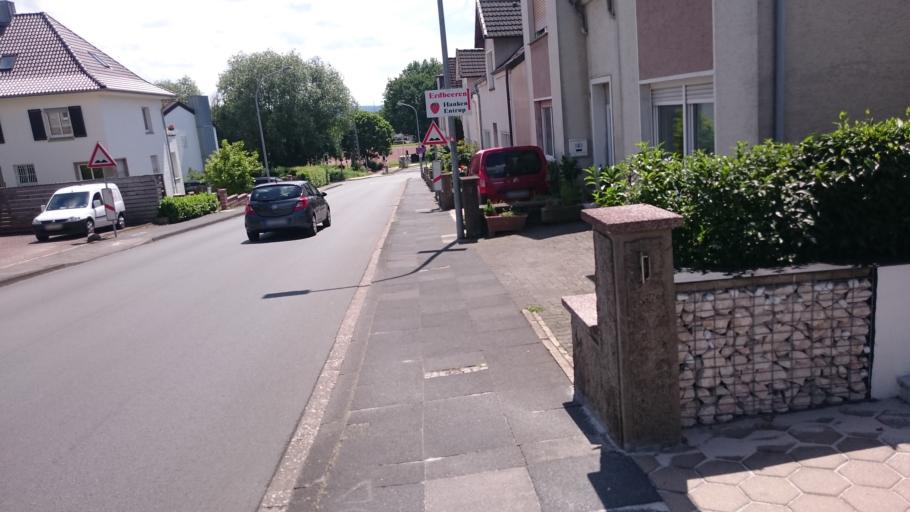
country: DE
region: North Rhine-Westphalia
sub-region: Regierungsbezirk Detmold
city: Lage
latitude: 51.9968
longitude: 8.7948
